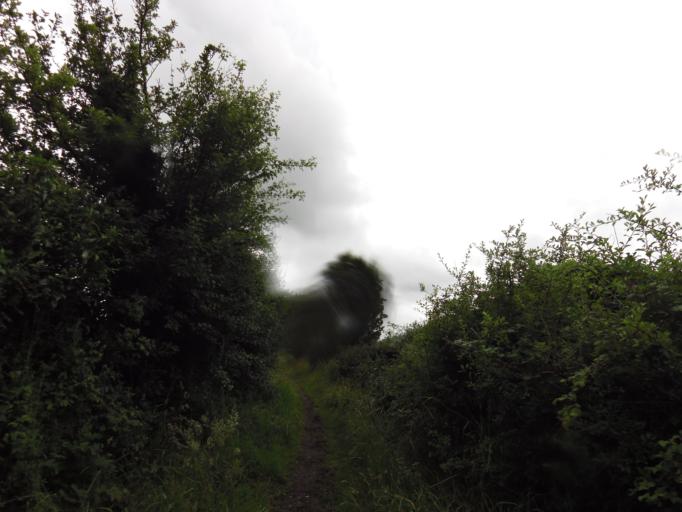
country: IE
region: Connaught
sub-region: County Galway
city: Athenry
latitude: 53.2860
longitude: -8.7104
